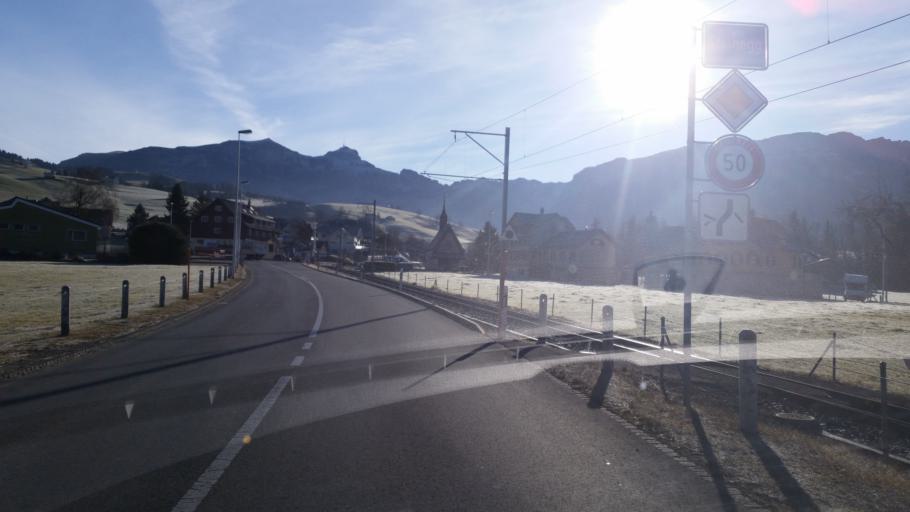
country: CH
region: Appenzell Innerrhoden
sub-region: Appenzell Inner Rhodes
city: Appenzell
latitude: 47.3218
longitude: 9.4285
